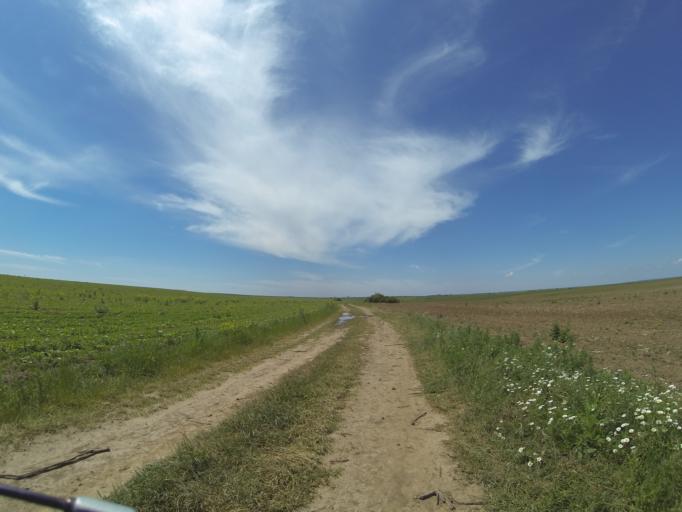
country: RO
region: Dolj
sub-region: Comuna Teslui
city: Teslui
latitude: 44.1907
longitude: 24.1525
